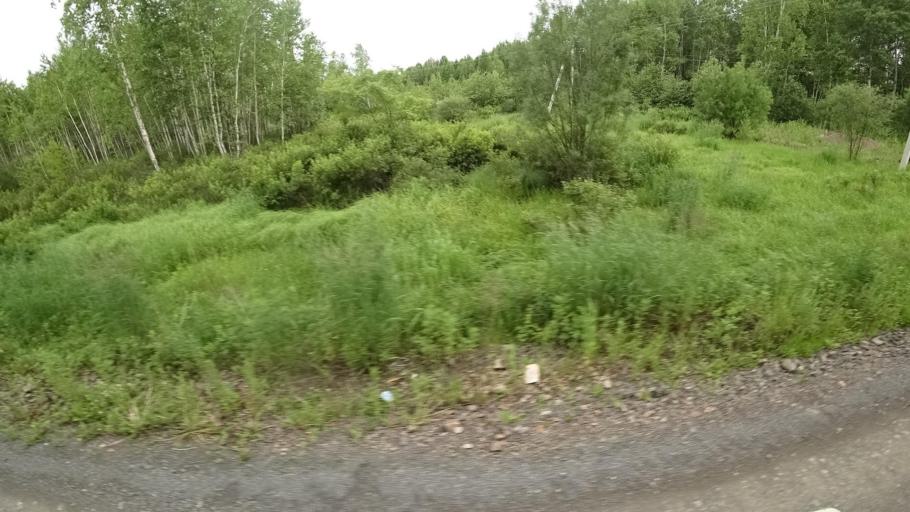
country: RU
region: Khabarovsk Krai
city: Amursk
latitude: 49.9051
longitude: 136.1393
